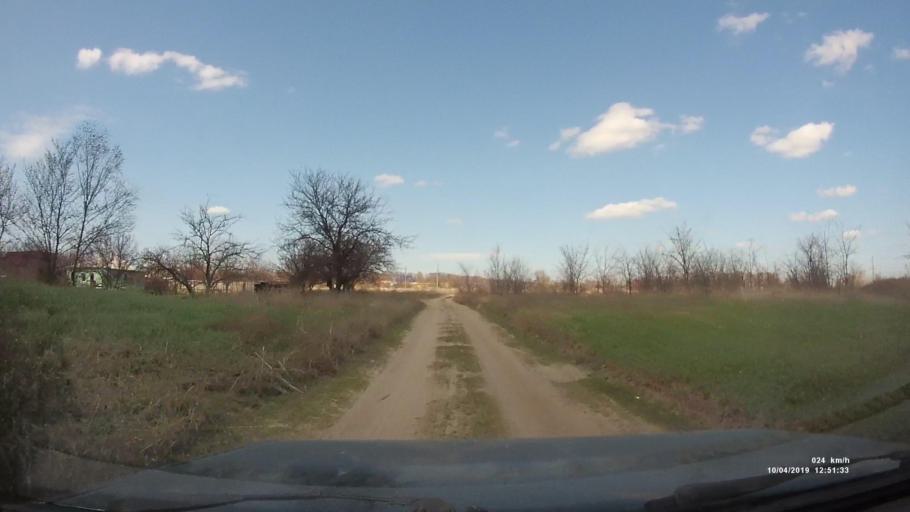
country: RU
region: Rostov
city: Kamensk-Shakhtinskiy
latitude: 48.3598
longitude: 40.2169
